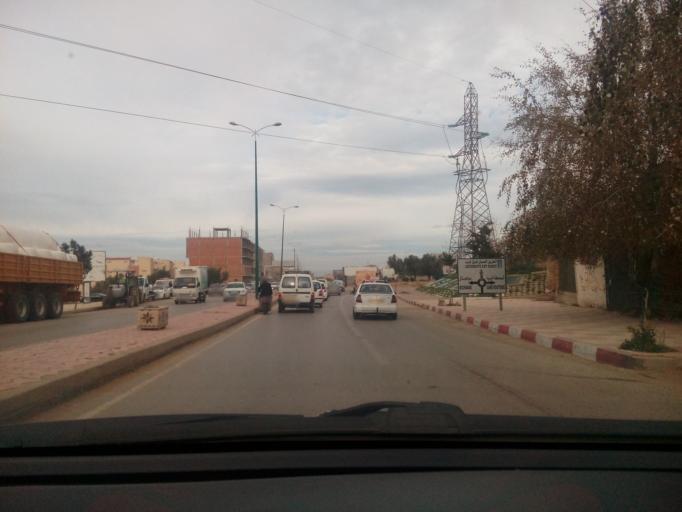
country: DZ
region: Tlemcen
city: Mansoura
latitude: 34.8841
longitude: -1.3515
